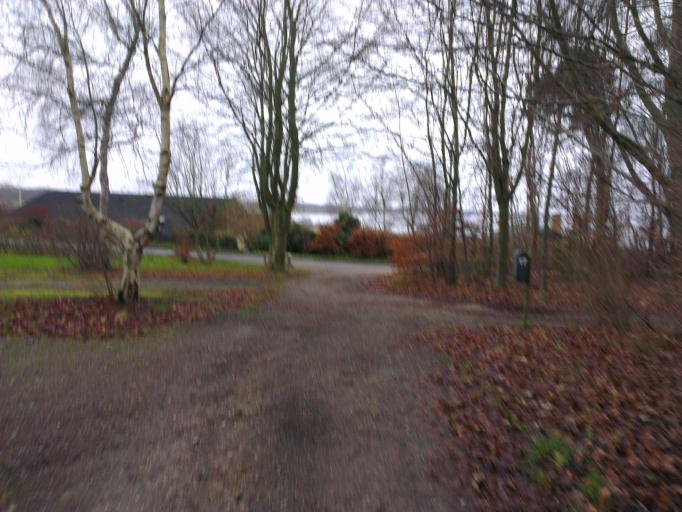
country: DK
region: Capital Region
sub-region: Frederikssund Kommune
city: Jaegerspris
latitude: 55.8530
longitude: 12.0052
